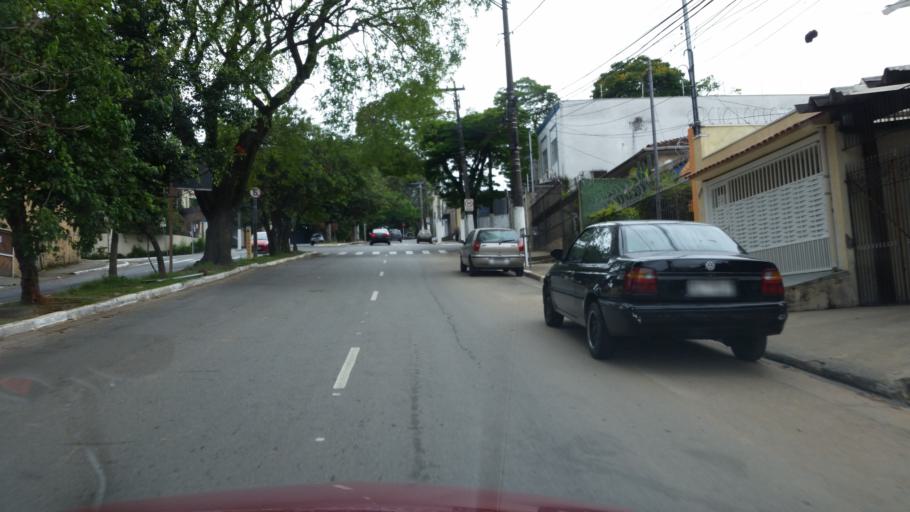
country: BR
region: Sao Paulo
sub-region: Diadema
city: Diadema
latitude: -23.6394
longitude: -46.6598
